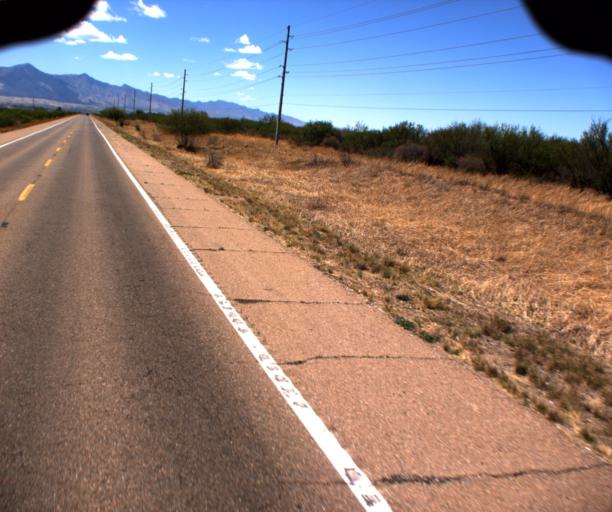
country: US
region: Arizona
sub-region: Cochise County
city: Naco
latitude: 31.3781
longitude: -110.0239
